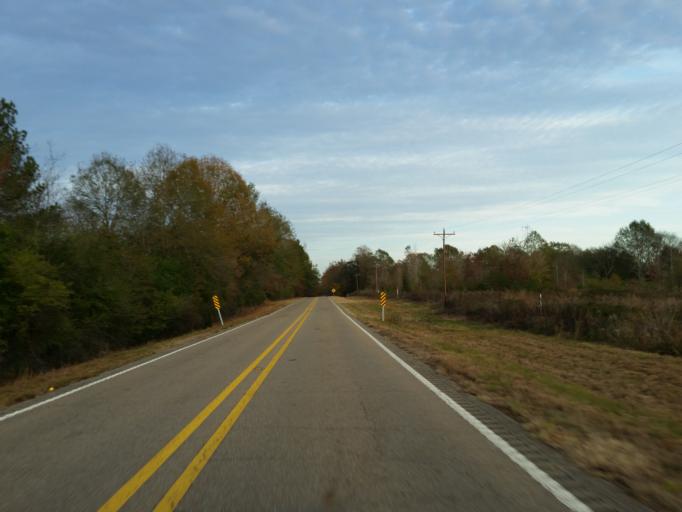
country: US
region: Mississippi
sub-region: Lauderdale County
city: Marion
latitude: 32.4245
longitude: -88.4713
